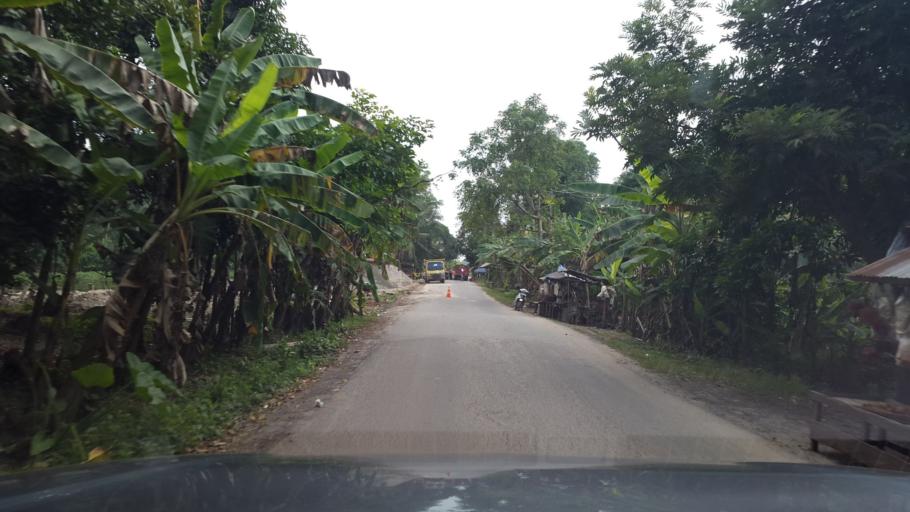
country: ID
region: South Sumatra
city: Tanjung Lubuk
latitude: -3.2651
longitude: 104.8688
